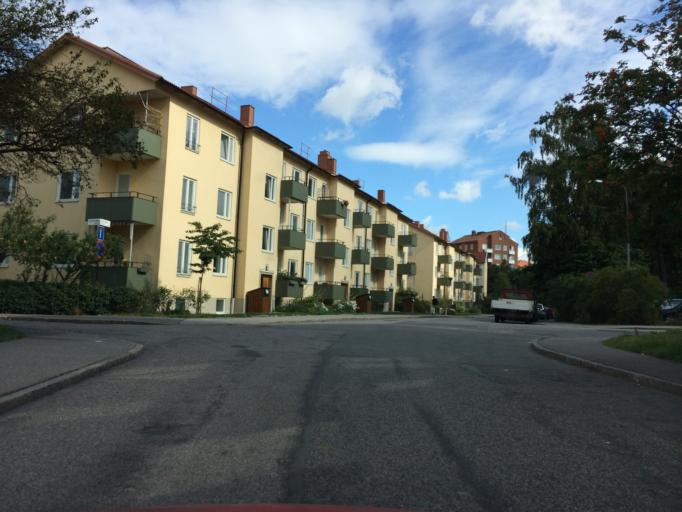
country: SE
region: Stockholm
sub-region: Huddinge Kommun
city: Segeltorp
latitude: 59.2986
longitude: 17.9792
